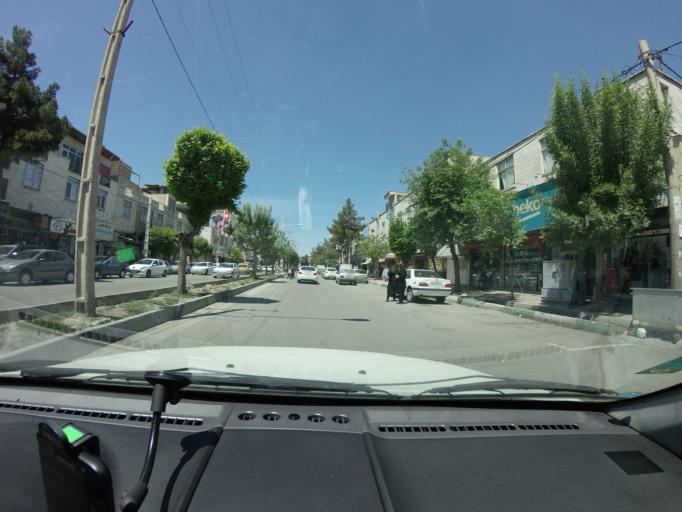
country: IR
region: Tehran
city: Eslamshahr
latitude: 35.5292
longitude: 51.2246
